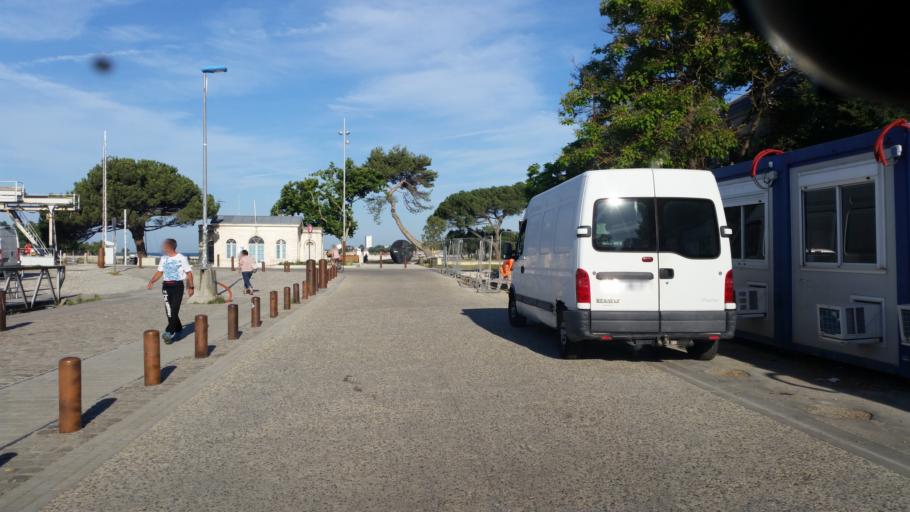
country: FR
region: Poitou-Charentes
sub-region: Departement de la Charente-Maritime
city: La Rochelle
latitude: 46.1549
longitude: -1.1521
